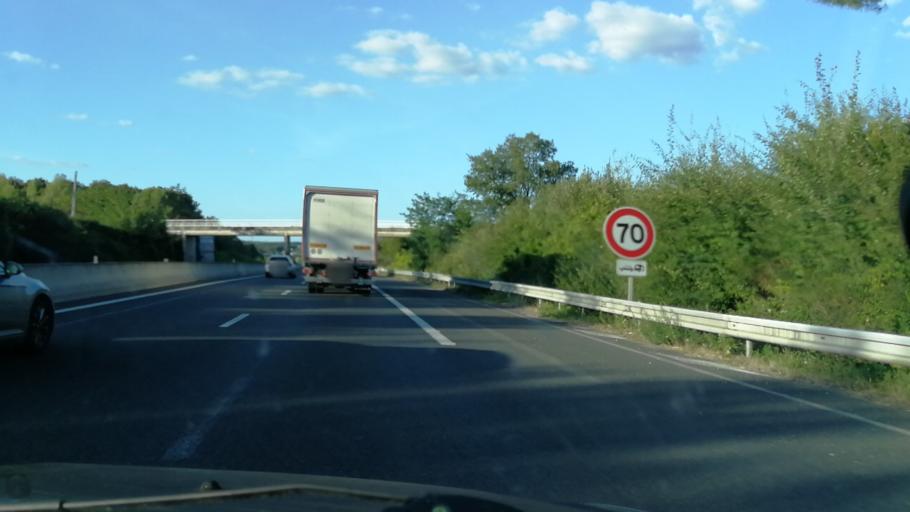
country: FR
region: Centre
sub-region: Departement d'Indre-et-Loire
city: Montbazon
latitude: 47.2752
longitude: 0.6765
